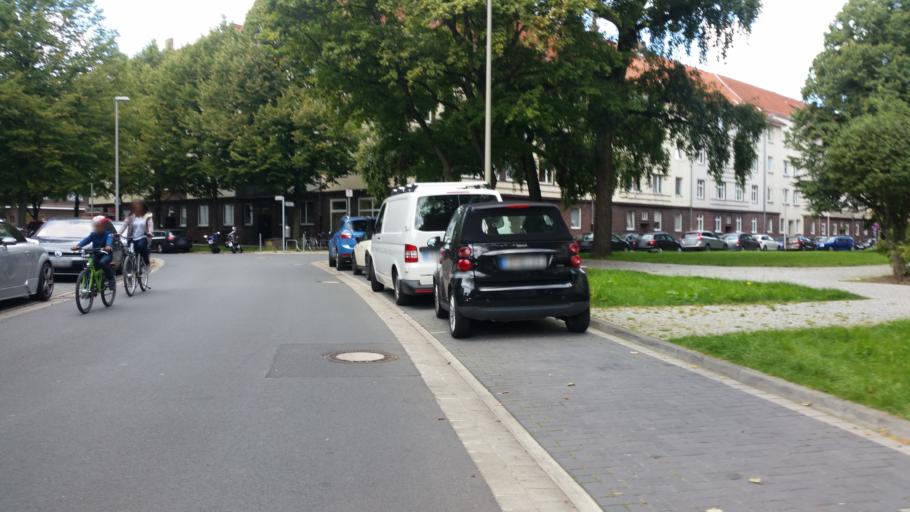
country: DE
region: Lower Saxony
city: Hannover
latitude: 52.4003
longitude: 9.7794
